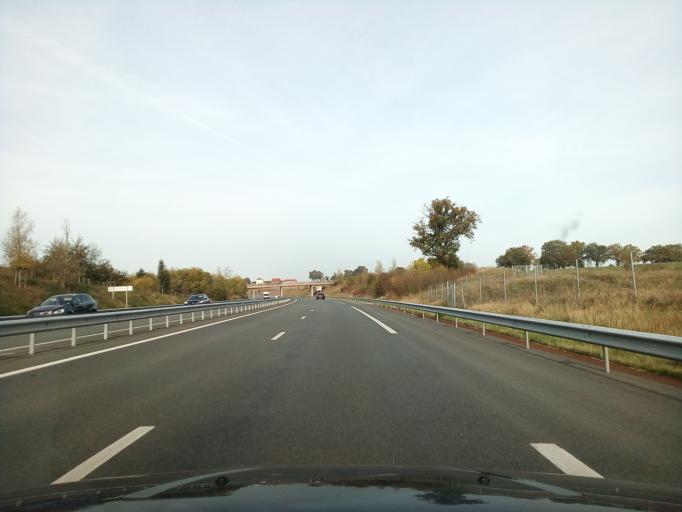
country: FR
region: Rhone-Alpes
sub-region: Departement de la Loire
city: La Pacaudiere
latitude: 46.1793
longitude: 3.8782
